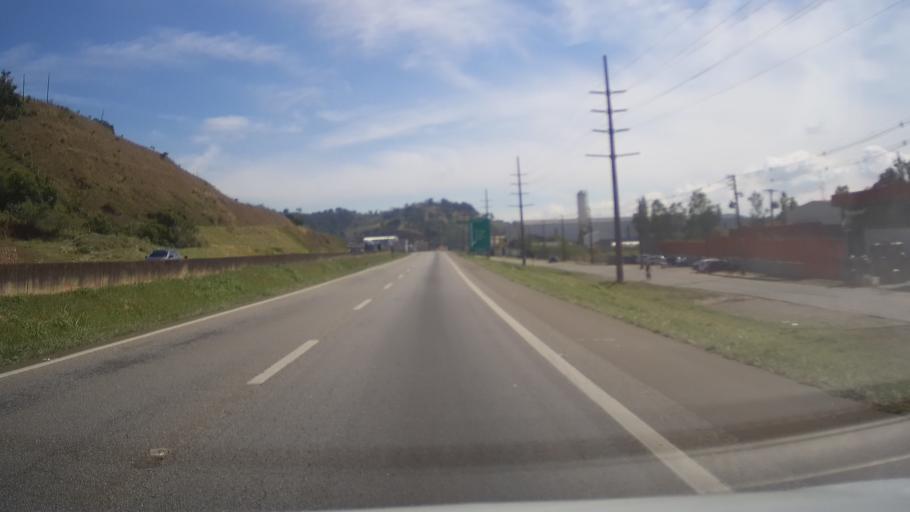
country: BR
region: Minas Gerais
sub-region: Cambui
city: Cambui
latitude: -22.6009
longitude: -46.0580
